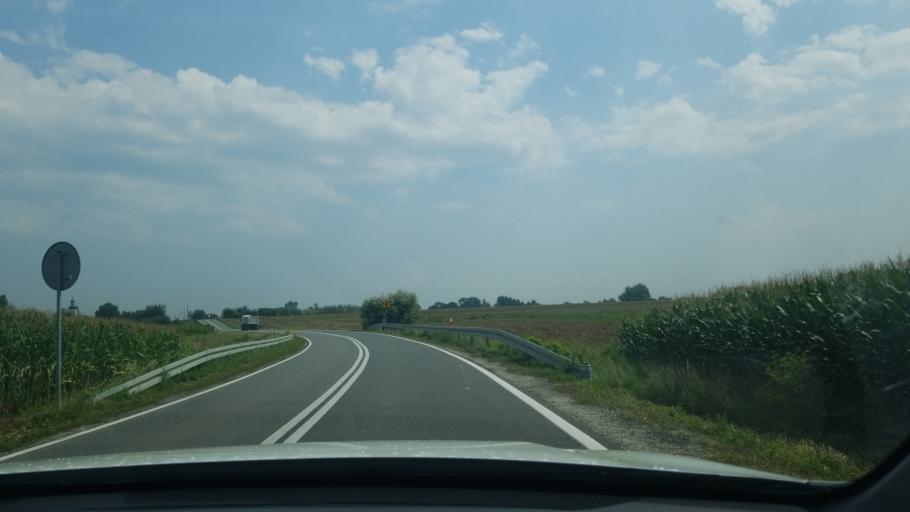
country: PL
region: Lesser Poland Voivodeship
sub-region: Powiat bochenski
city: Dziewin
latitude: 50.1180
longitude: 20.5041
